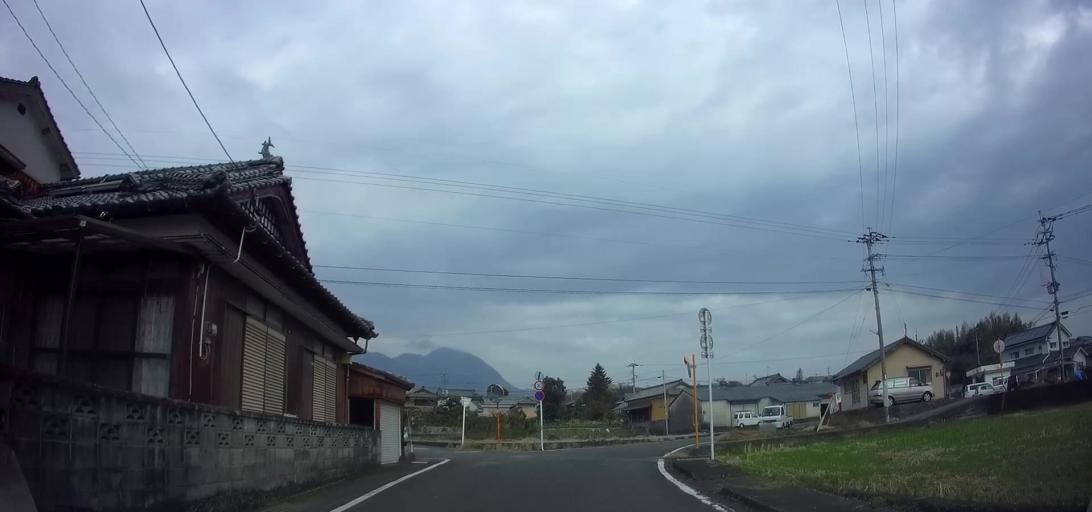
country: JP
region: Nagasaki
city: Shimabara
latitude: 32.6744
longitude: 130.3021
